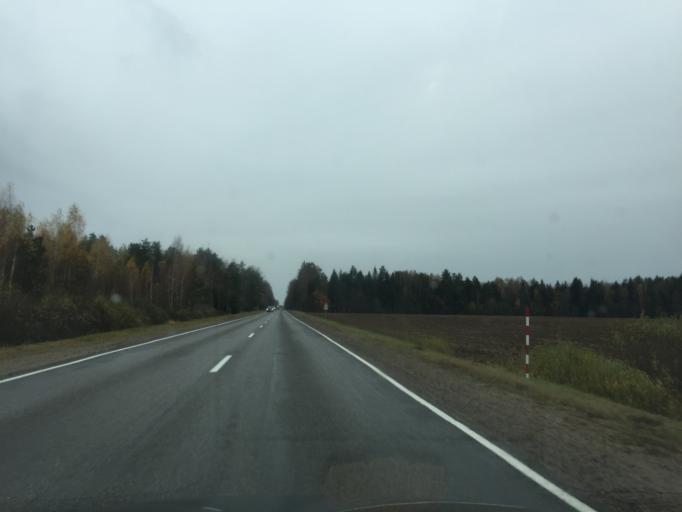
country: BY
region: Mogilev
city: Chavusy
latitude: 53.7268
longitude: 31.1224
